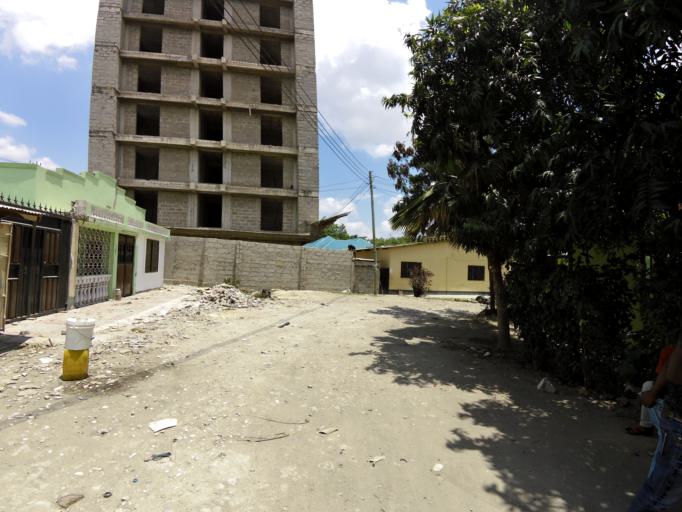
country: TZ
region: Dar es Salaam
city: Dar es Salaam
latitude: -6.8276
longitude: 39.2529
